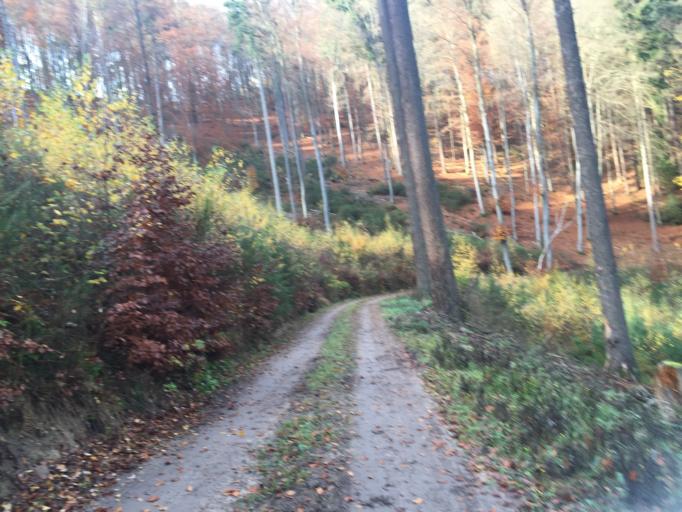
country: DE
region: Rheinland-Pfalz
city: Altleiningen
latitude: 49.4822
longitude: 8.0651
